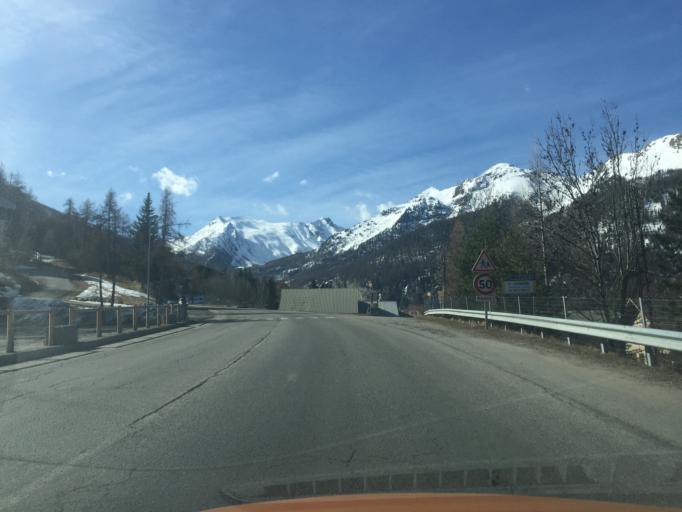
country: FR
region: Provence-Alpes-Cote d'Azur
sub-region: Departement des Hautes-Alpes
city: Embrun
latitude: 44.4969
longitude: 6.5546
